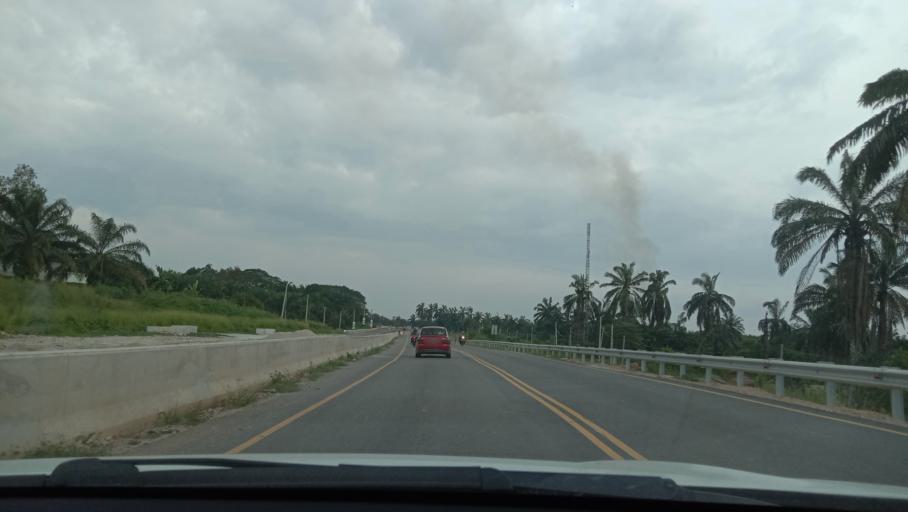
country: MY
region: Selangor
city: Batu Arang
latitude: 3.2686
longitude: 101.4548
